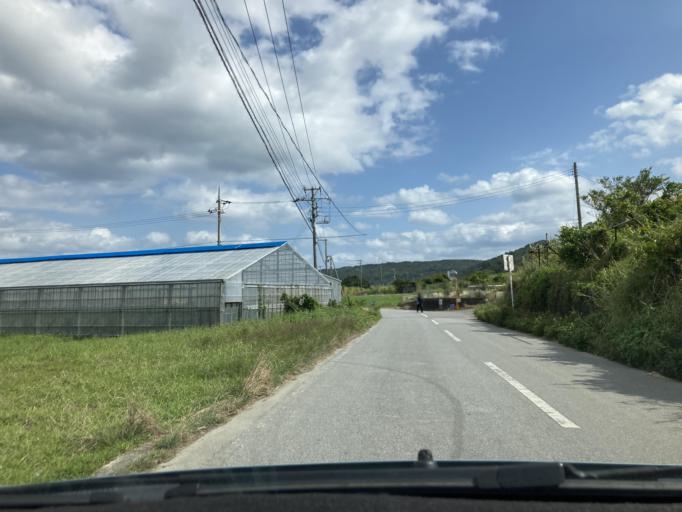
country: JP
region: Okinawa
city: Ginowan
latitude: 26.1690
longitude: 127.7773
